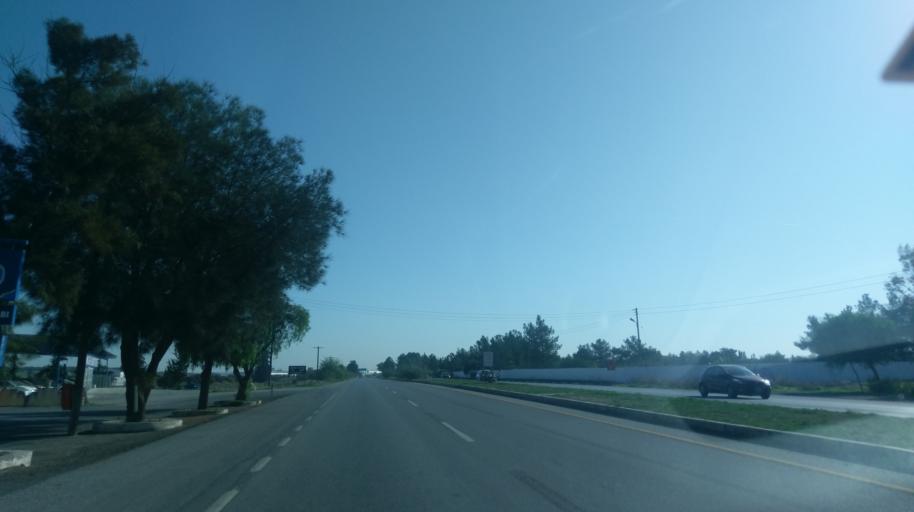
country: CY
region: Larnaka
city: Athienou
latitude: 35.2090
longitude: 33.5809
